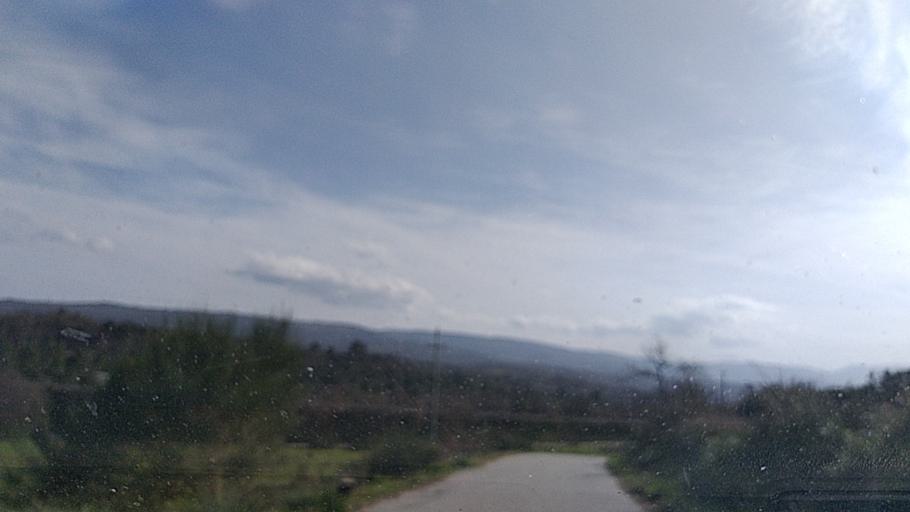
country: PT
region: Guarda
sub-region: Celorico da Beira
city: Celorico da Beira
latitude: 40.6448
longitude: -7.4284
